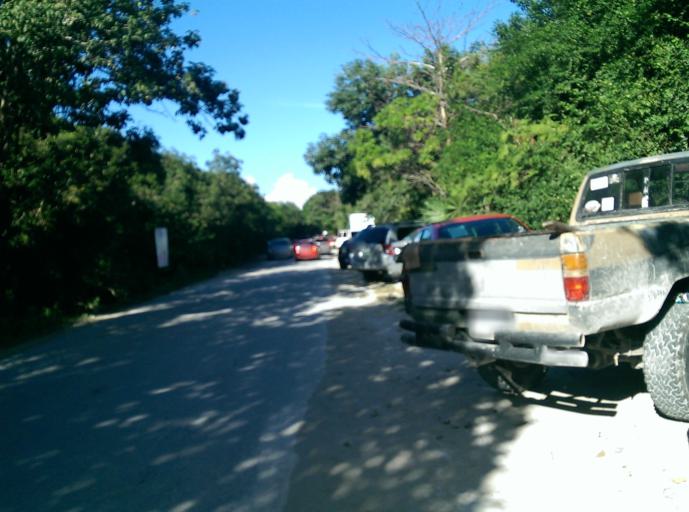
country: MX
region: Quintana Roo
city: Tulum
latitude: 20.2028
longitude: -87.4343
